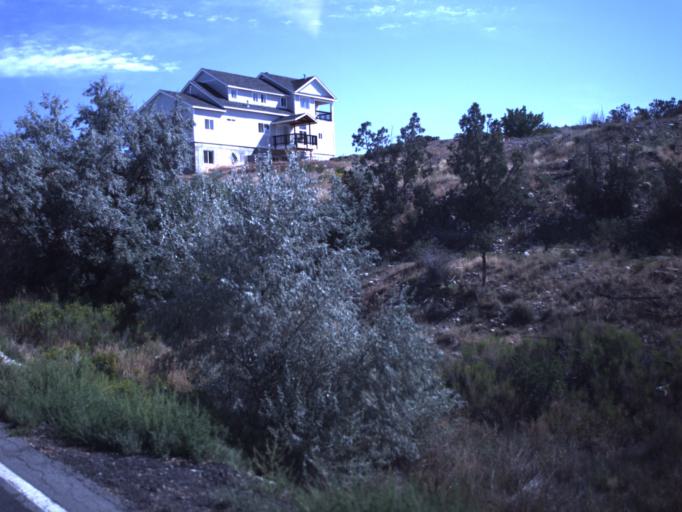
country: US
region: Utah
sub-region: Duchesne County
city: Duchesne
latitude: 40.1758
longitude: -110.4006
